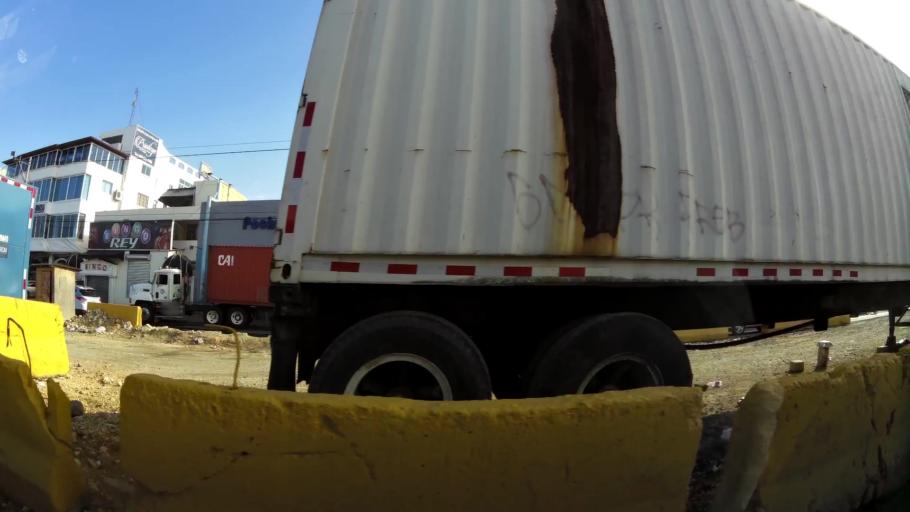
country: DO
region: Santo Domingo
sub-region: Santo Domingo
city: Santo Domingo Este
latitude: 18.5017
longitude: -69.8537
